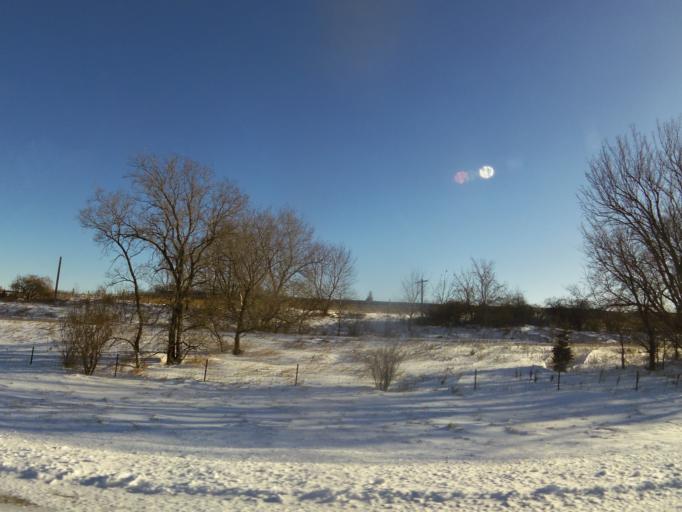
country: US
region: Minnesota
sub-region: Rice County
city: Faribault
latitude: 44.2359
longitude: -93.2789
